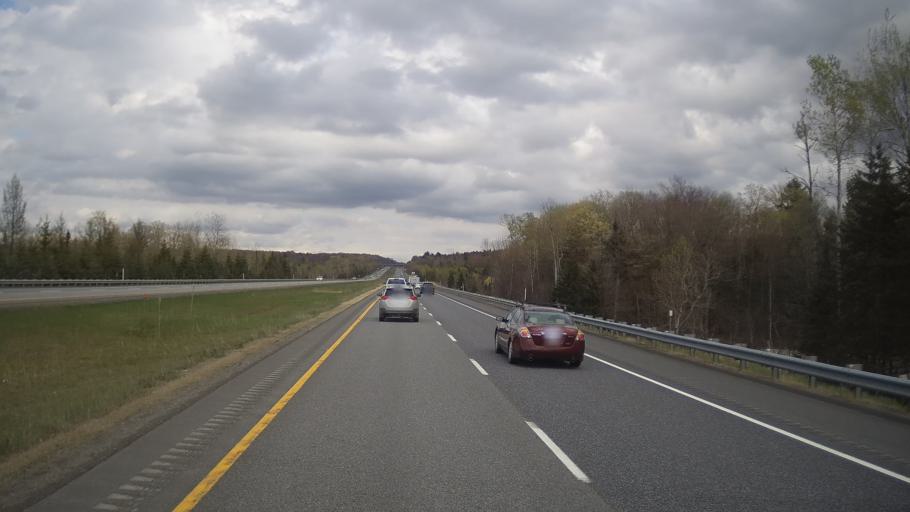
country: CA
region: Quebec
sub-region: Monteregie
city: Waterloo
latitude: 45.3014
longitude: -72.4411
